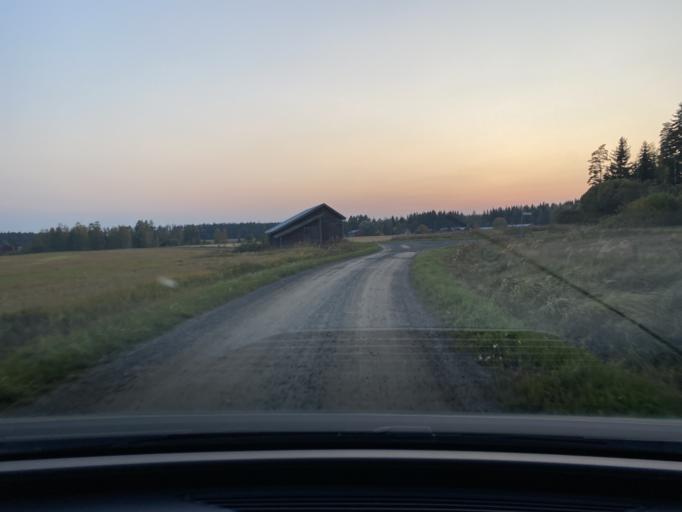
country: FI
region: Pirkanmaa
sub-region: Lounais-Pirkanmaa
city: Punkalaidun
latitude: 61.1157
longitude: 23.2447
